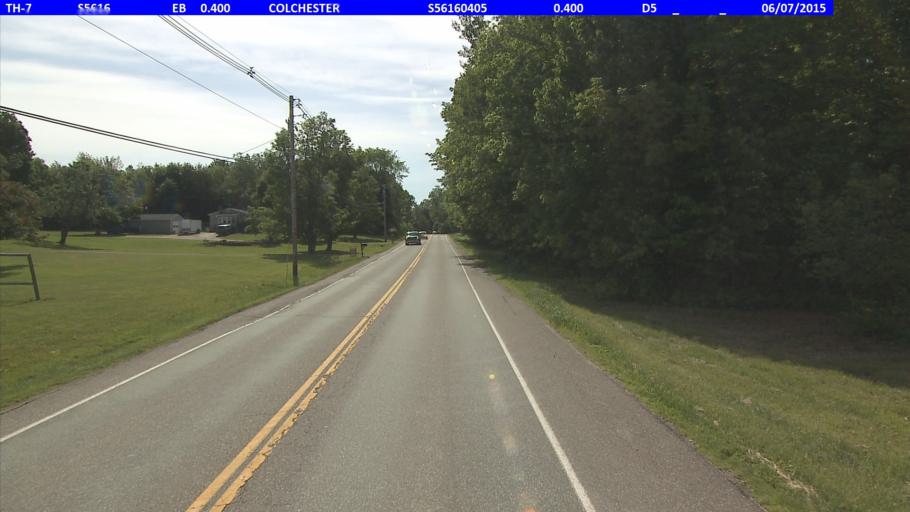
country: US
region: Vermont
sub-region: Chittenden County
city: Colchester
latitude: 44.5261
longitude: -73.1651
